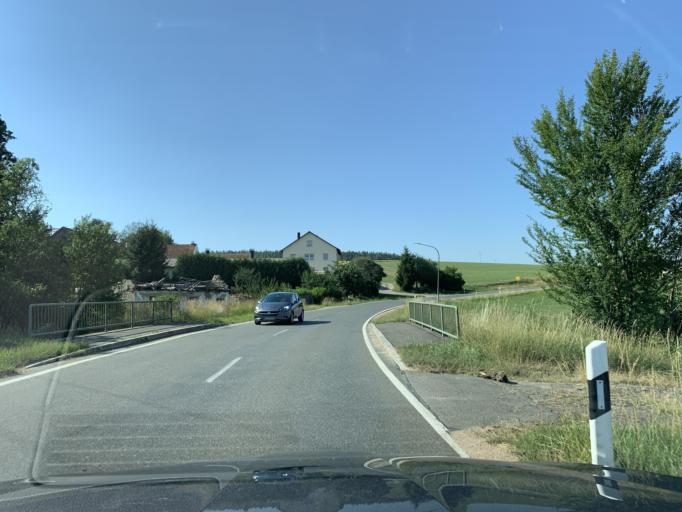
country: DE
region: Bavaria
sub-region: Upper Palatinate
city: Schwarzhofen
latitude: 49.3873
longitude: 12.3539
